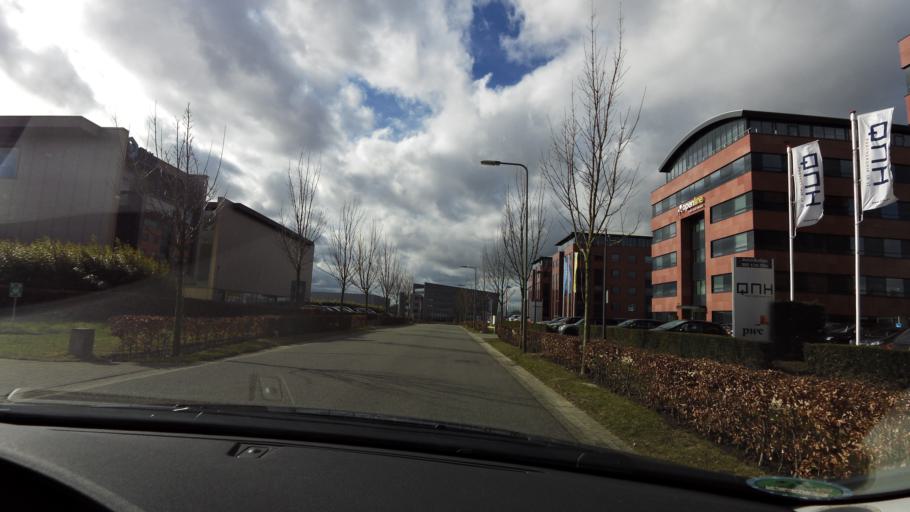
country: NL
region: Limburg
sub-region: Gemeente Beek
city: Beek
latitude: 50.9305
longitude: 5.7812
